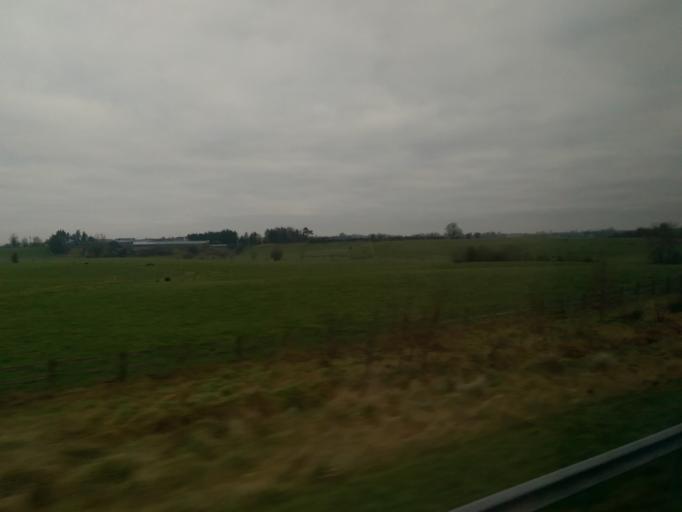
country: IE
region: Connaught
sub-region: County Galway
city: Loughrea
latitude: 53.2838
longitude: -8.4957
